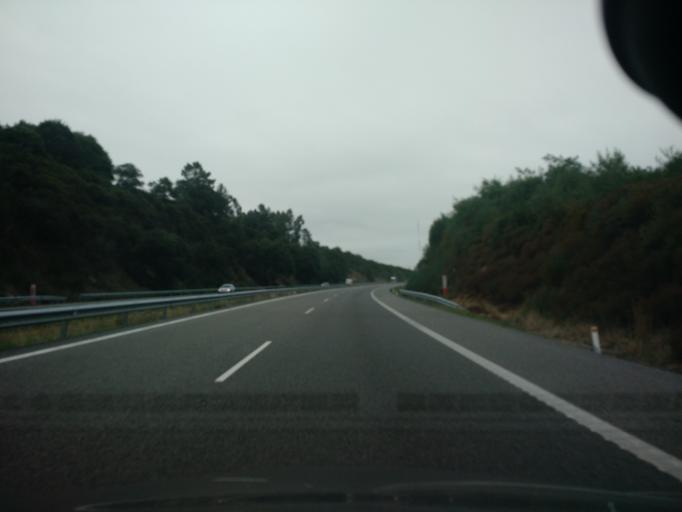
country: ES
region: Galicia
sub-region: Provincia da Coruna
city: Santiago de Compostela
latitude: 42.9079
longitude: -8.4815
